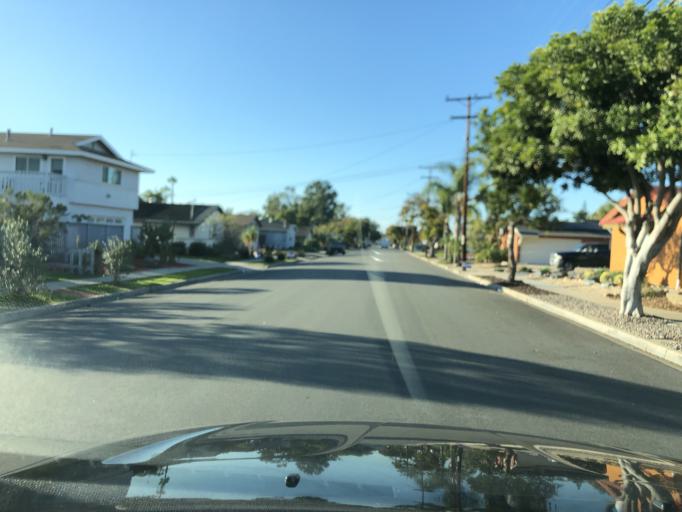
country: US
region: California
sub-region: San Diego County
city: La Jolla
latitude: 32.8216
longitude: -117.1884
